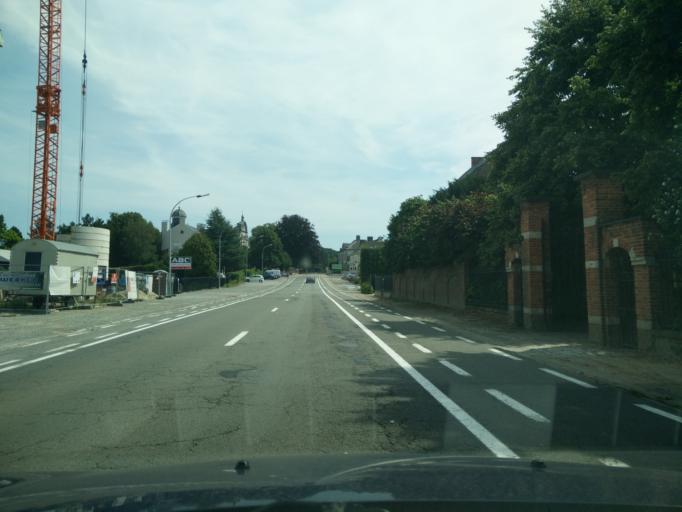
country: BE
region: Flanders
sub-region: Provincie Oost-Vlaanderen
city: Ninove
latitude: 50.8263
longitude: 4.0377
